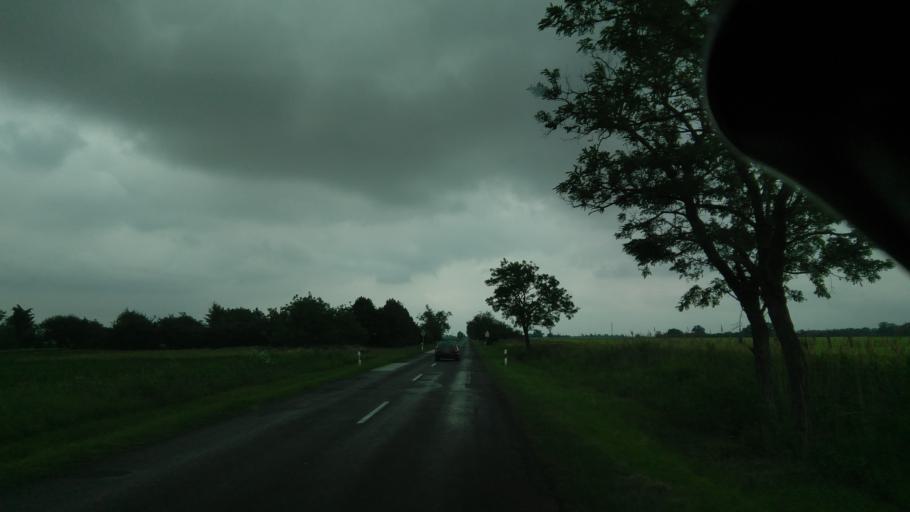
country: HU
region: Bekes
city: Szabadkigyos
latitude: 46.6270
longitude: 21.1052
